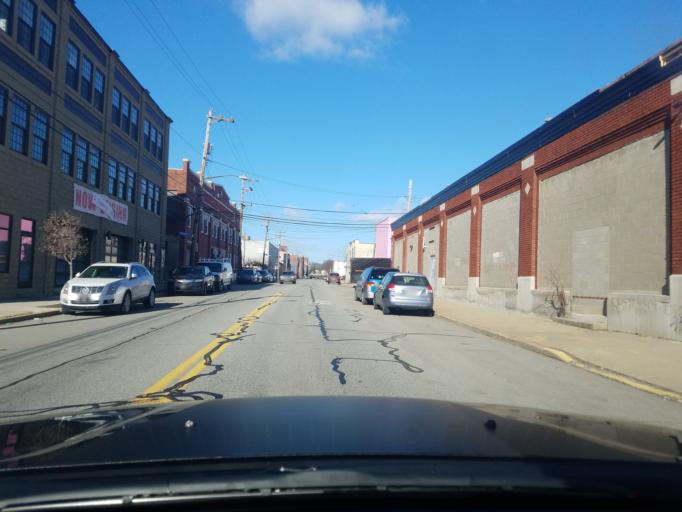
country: US
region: Pennsylvania
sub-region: Allegheny County
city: Wilkinsburg
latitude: 40.4578
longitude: -79.9104
